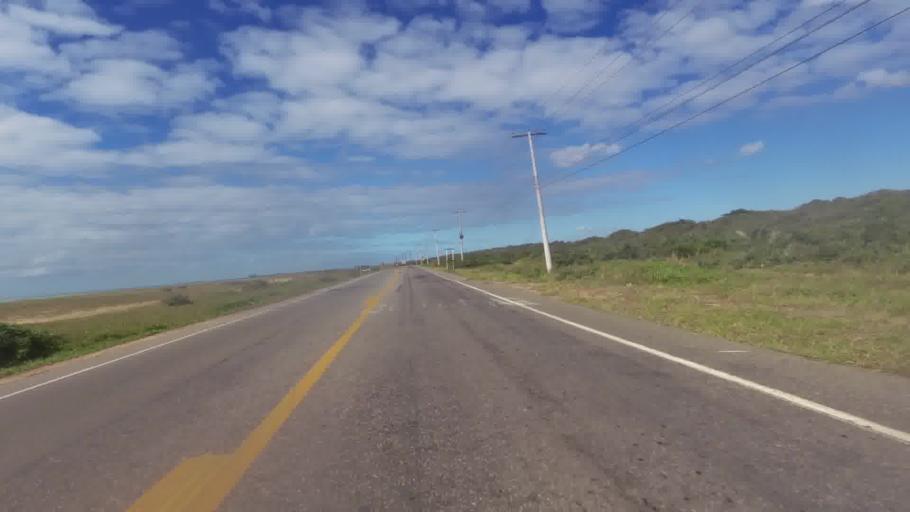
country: BR
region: Espirito Santo
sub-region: Itapemirim
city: Itapemirim
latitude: -20.9606
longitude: -40.8099
